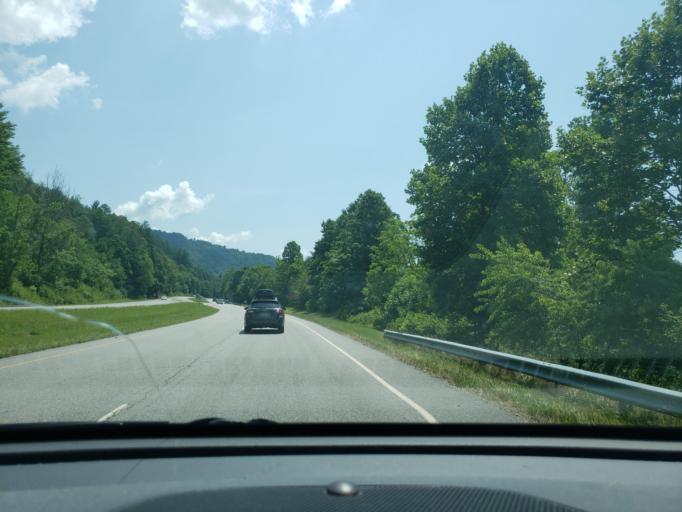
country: US
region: North Carolina
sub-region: Wilkes County
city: Millers Creek
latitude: 36.1808
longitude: -81.3941
